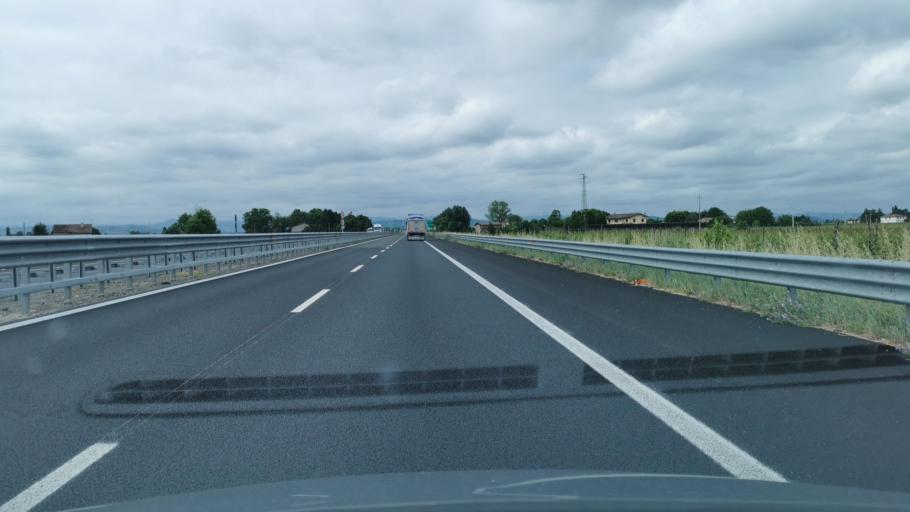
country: IT
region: Emilia-Romagna
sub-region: Provincia di Ravenna
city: Solarolo
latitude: 44.3634
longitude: 11.8269
